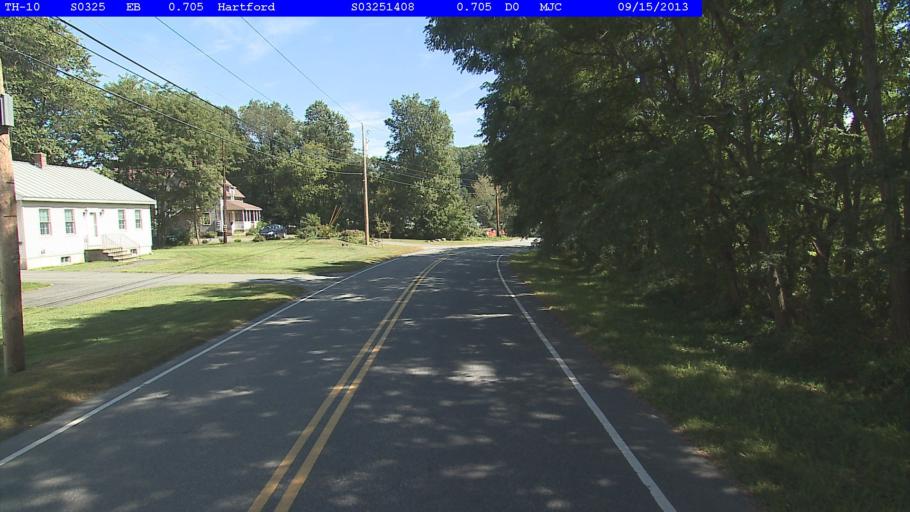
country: US
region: Vermont
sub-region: Windsor County
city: White River Junction
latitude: 43.6439
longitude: -72.3226
